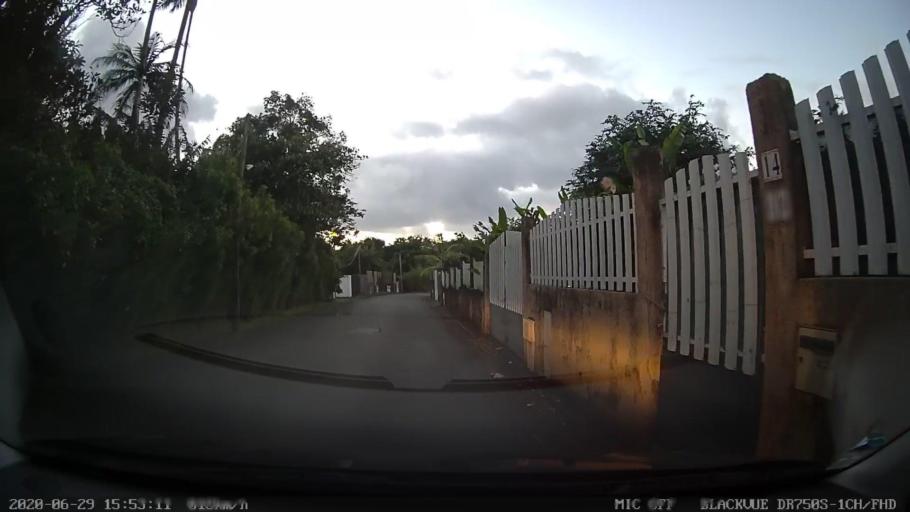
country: RE
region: Reunion
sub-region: Reunion
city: Bras-Panon
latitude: -20.9998
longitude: 55.6949
